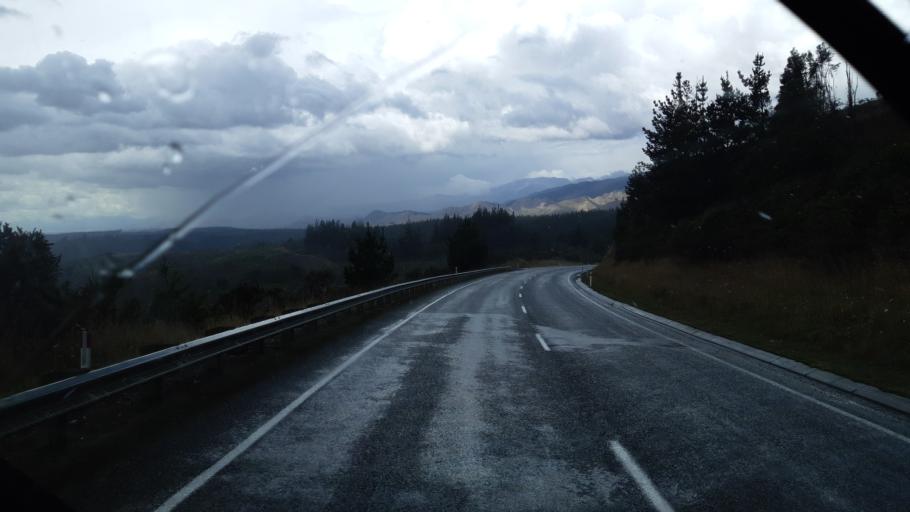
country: NZ
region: Tasman
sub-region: Tasman District
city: Wakefield
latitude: -41.4788
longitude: 172.9209
